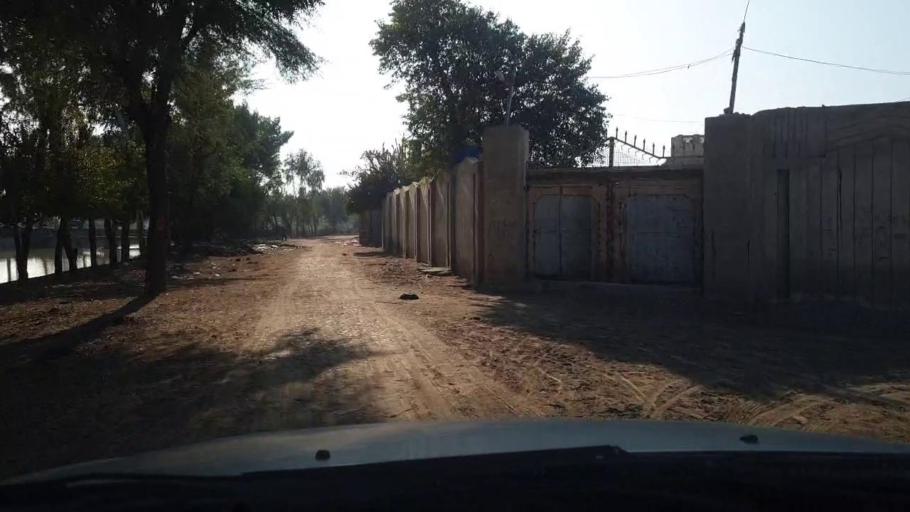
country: PK
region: Sindh
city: Mirpur Mathelo
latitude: 27.9825
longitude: 69.5402
